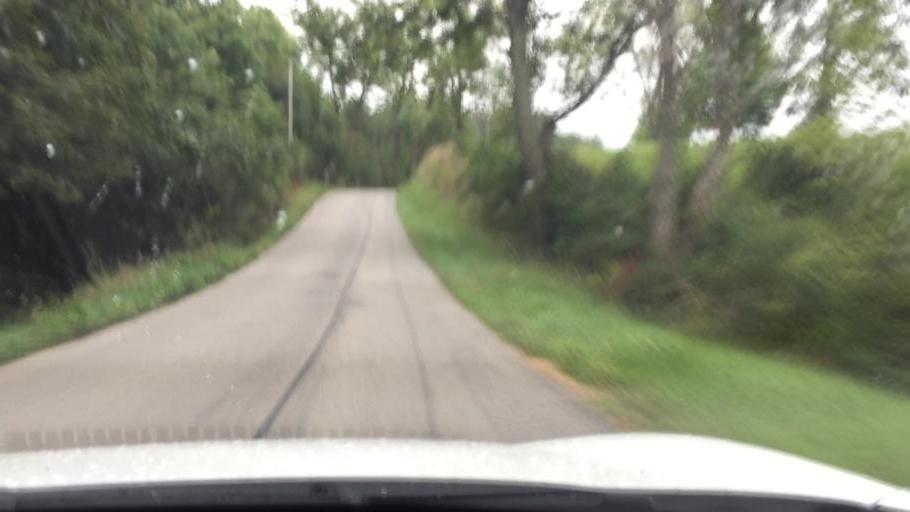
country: US
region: Ohio
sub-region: Champaign County
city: Mechanicsburg
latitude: 40.0042
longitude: -83.6548
